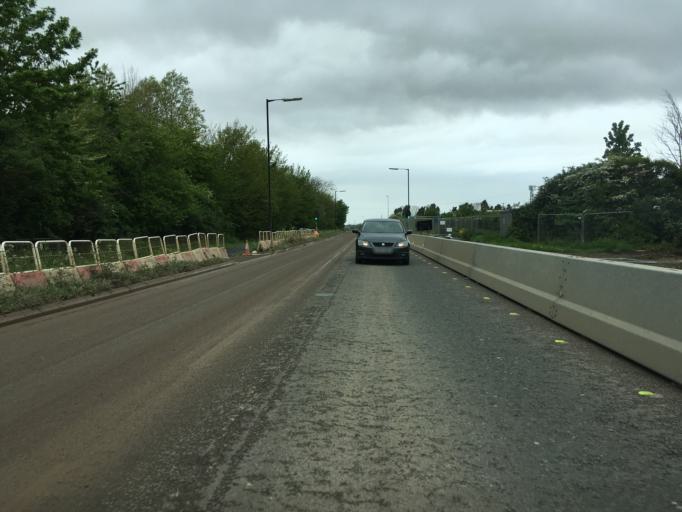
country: GB
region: England
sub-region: North Somerset
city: Hutton
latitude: 51.3361
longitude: -2.9116
